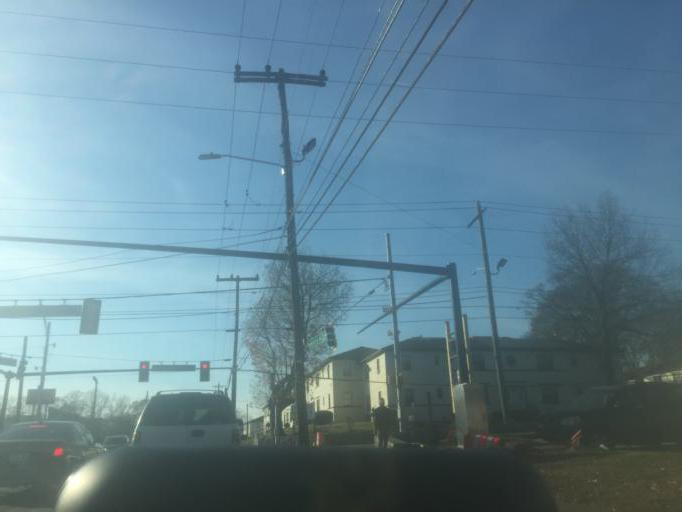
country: US
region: Georgia
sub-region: Fulton County
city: Atlanta
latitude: 33.7222
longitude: -84.4075
